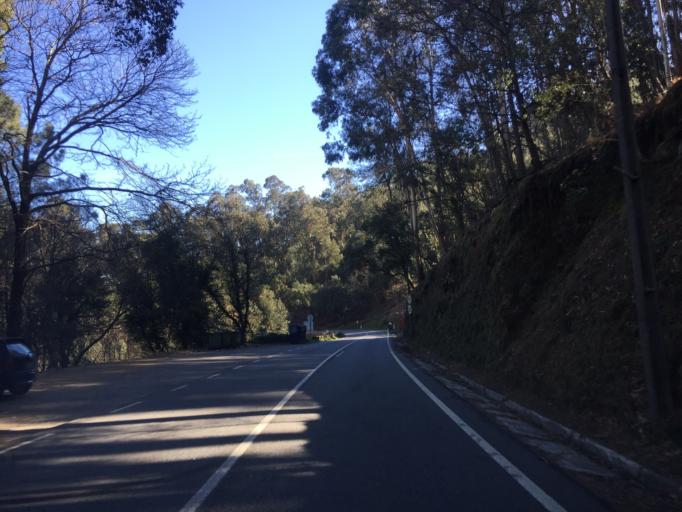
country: PT
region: Aveiro
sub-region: Vale de Cambra
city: Macieira de Cambra
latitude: 40.8901
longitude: -8.3422
